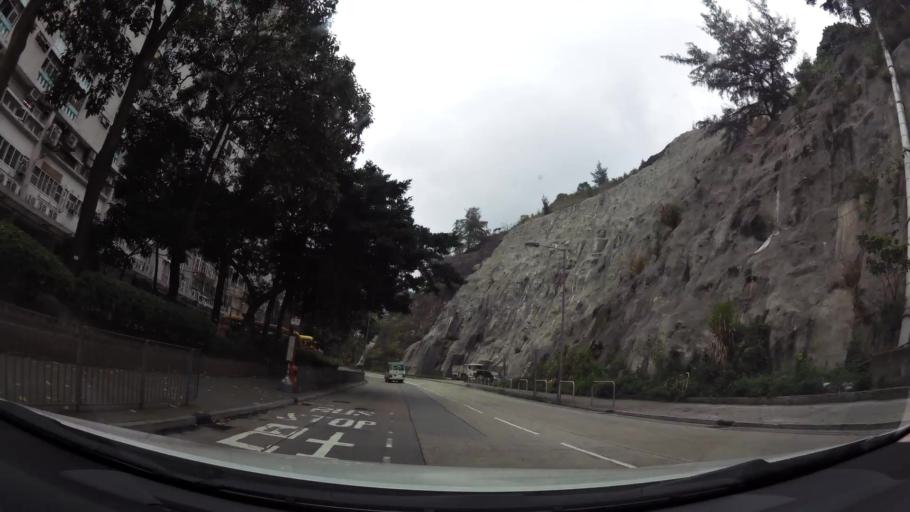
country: HK
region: Kowloon City
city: Kowloon
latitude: 22.3299
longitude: 114.2272
